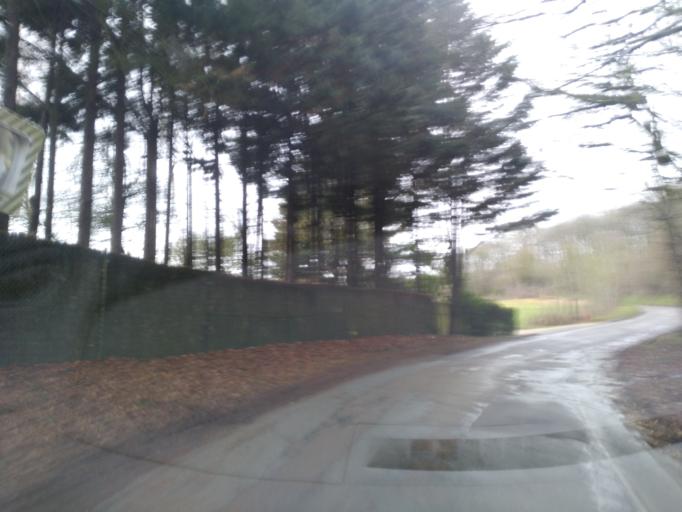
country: FR
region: Ile-de-France
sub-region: Departement des Yvelines
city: Chavenay
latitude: 48.8738
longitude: 2.0012
